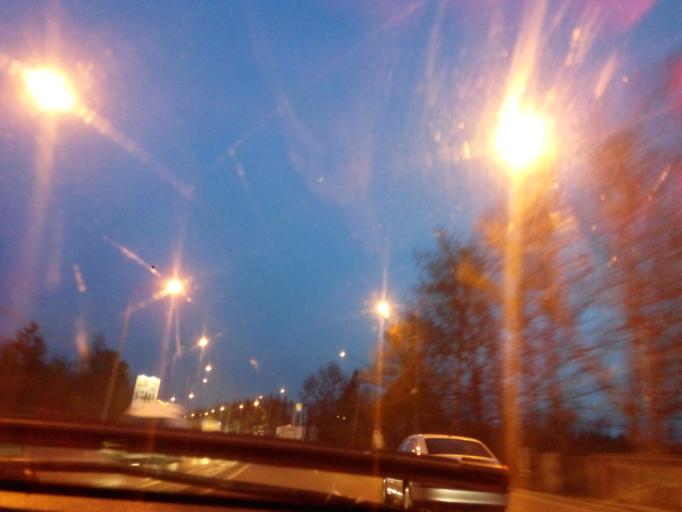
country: RO
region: Ilfov
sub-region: Comuna Otopeni
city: Otopeni
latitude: 44.5264
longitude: 26.0711
